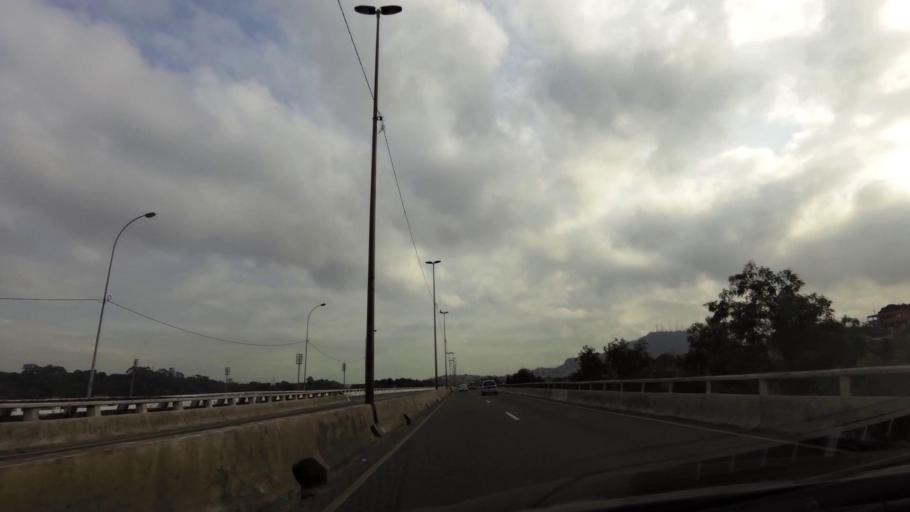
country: BR
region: Espirito Santo
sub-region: Vitoria
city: Vitoria
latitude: -20.3373
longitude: -40.3548
